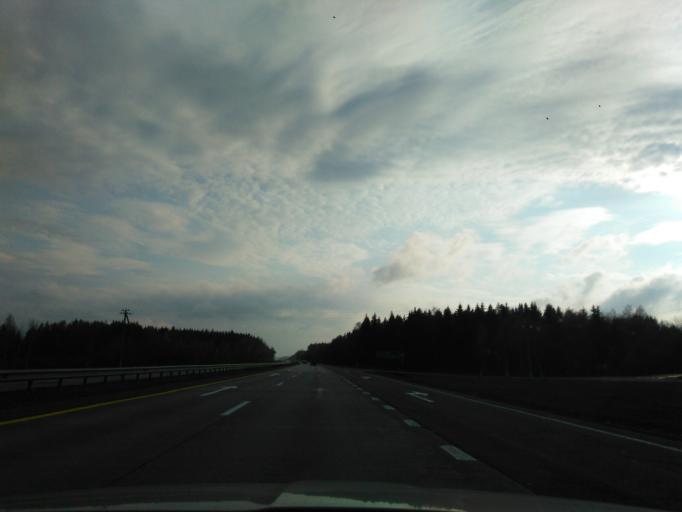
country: BY
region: Minsk
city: Astrashytski Haradok
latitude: 54.0927
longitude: 27.7730
